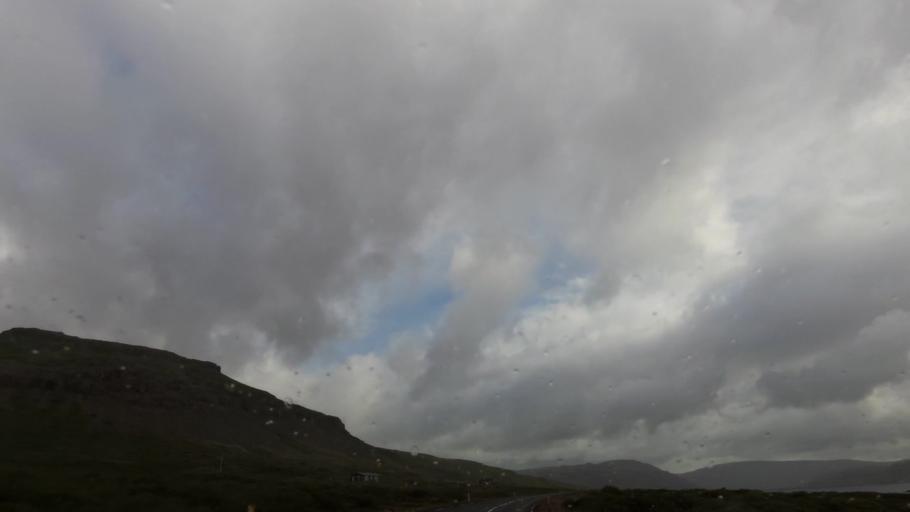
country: IS
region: Westfjords
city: Isafjoerdur
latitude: 65.5478
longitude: -23.2020
